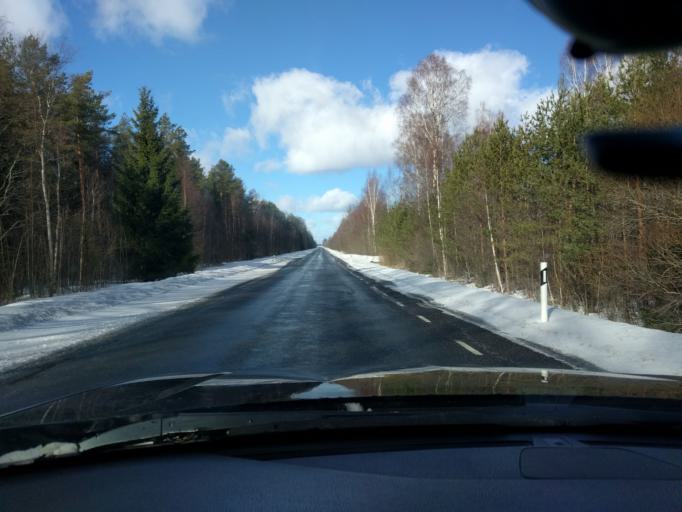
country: EE
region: Harju
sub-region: Anija vald
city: Kehra
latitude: 59.2353
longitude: 25.3819
